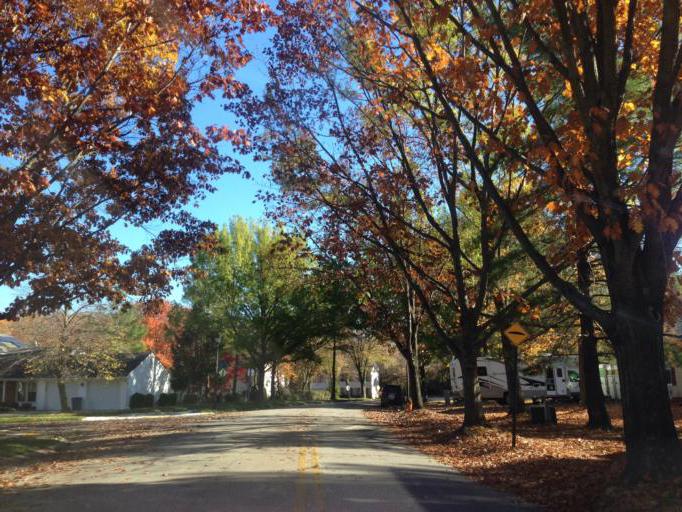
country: US
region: Maryland
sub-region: Howard County
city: Riverside
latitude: 39.2051
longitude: -76.8826
